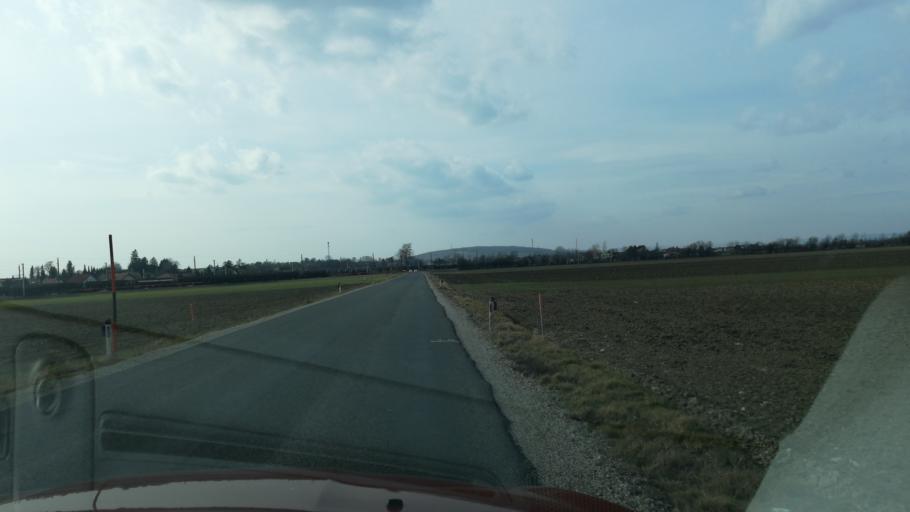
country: AT
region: Lower Austria
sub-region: Politischer Bezirk Tulln
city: Atzenbrugg
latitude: 48.3035
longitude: 15.9125
